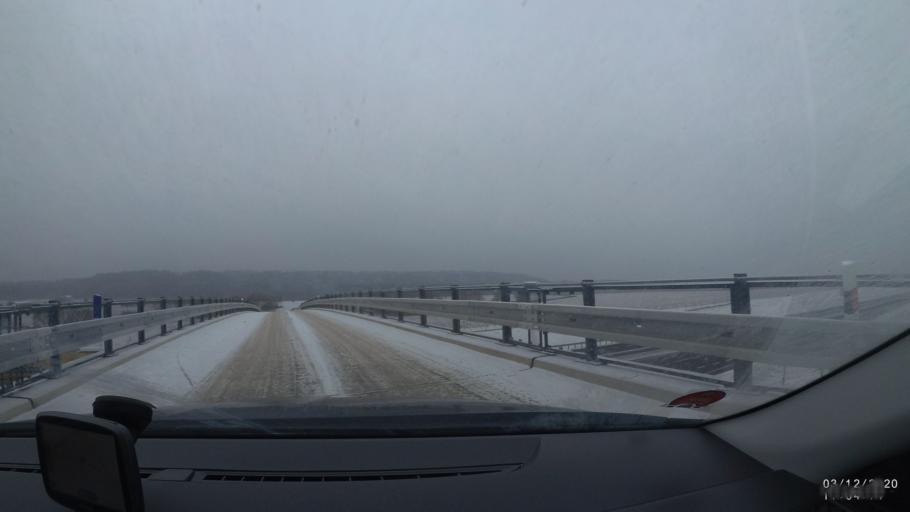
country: CZ
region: Central Bohemia
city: Revnicov
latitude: 50.1772
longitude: 13.8072
